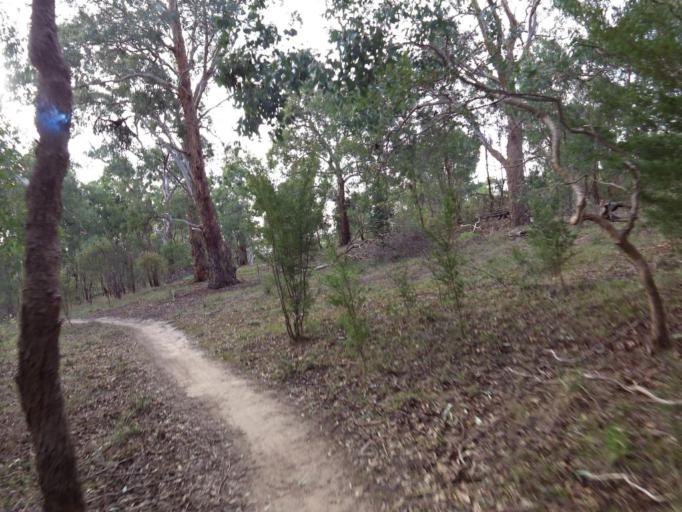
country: AU
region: Victoria
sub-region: Nillumbik
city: Eltham
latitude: -37.7412
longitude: 145.1450
